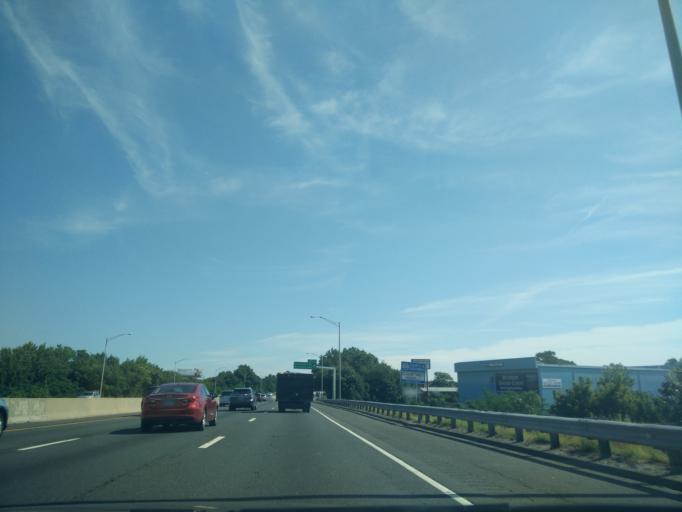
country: US
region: Connecticut
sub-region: Fairfield County
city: Stratford
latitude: 41.1790
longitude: -73.1473
